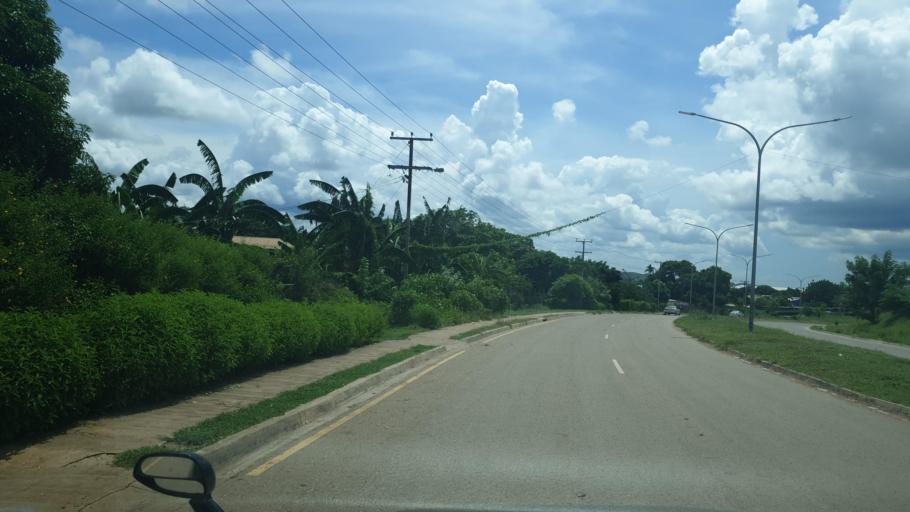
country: PG
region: National Capital
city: Port Moresby
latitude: -9.3769
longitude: 147.1539
